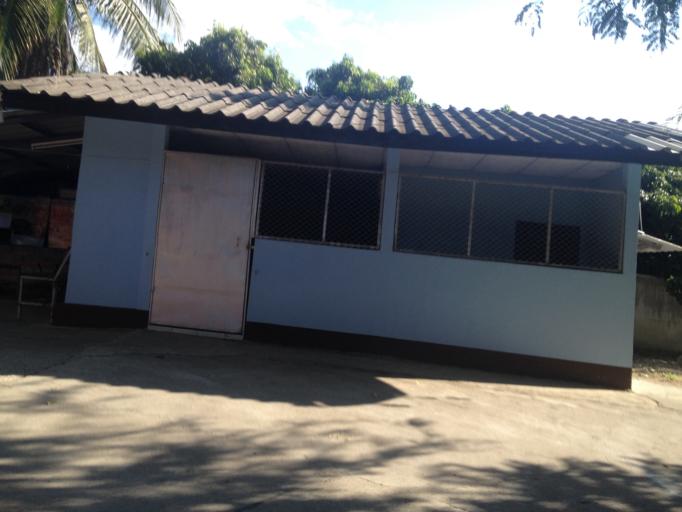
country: TH
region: Chiang Mai
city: Hang Dong
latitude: 18.6989
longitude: 98.9271
